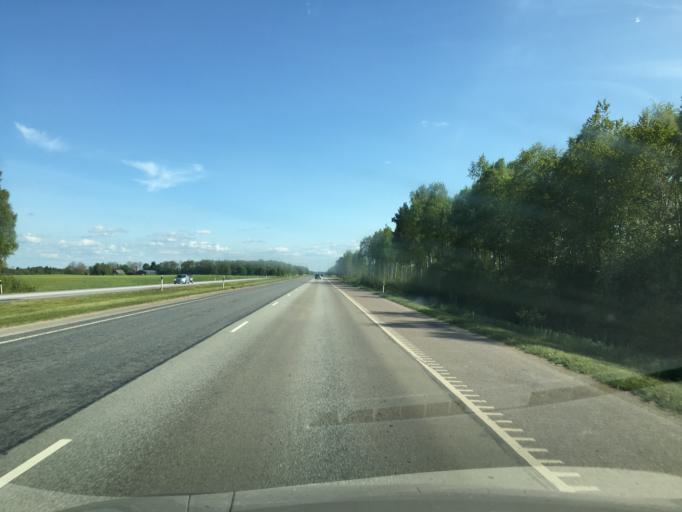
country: EE
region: Harju
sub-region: Rae vald
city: Jueri
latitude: 59.3328
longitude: 24.9111
